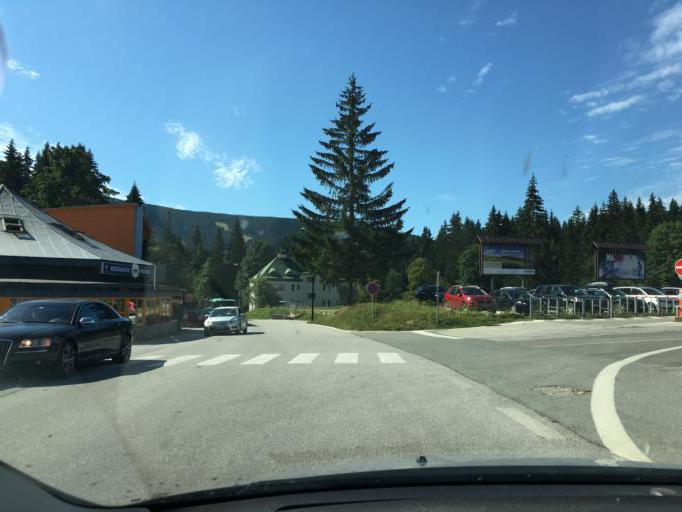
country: CZ
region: Kralovehradecky
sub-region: Okres Trutnov
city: Spindleruv Mlyn
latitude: 50.7343
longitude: 15.6086
